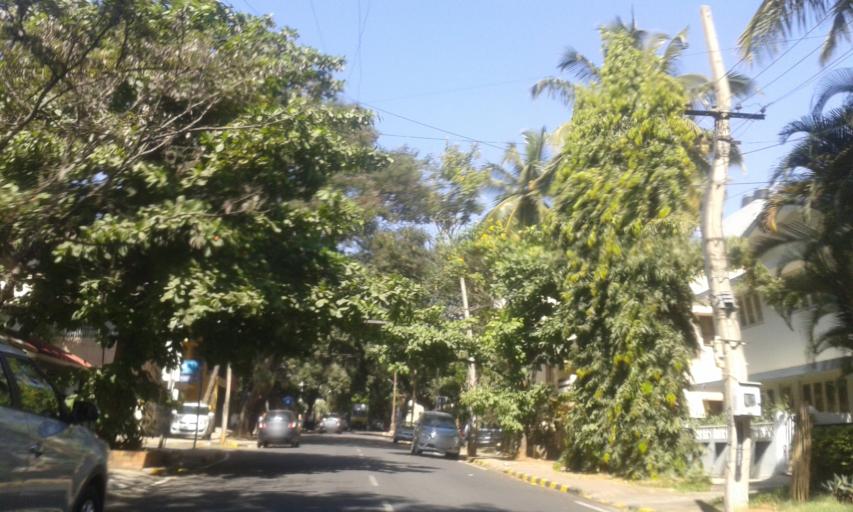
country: IN
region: Karnataka
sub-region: Bangalore Urban
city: Bangalore
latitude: 12.9225
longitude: 77.5915
